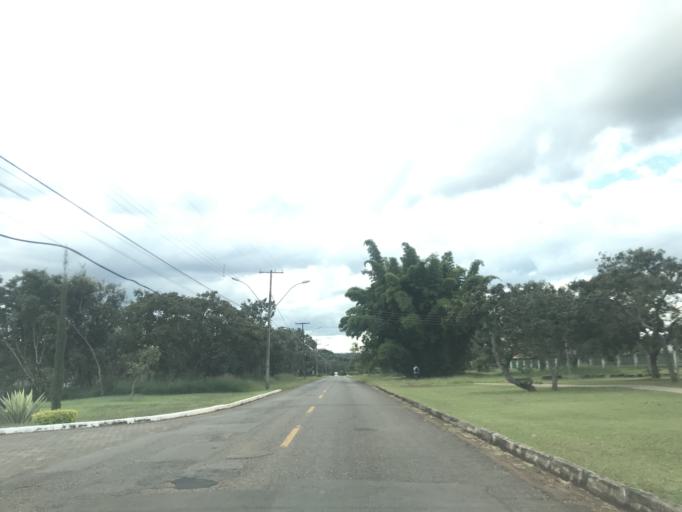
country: BR
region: Federal District
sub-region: Brasilia
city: Brasilia
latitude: -15.9007
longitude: -47.9389
